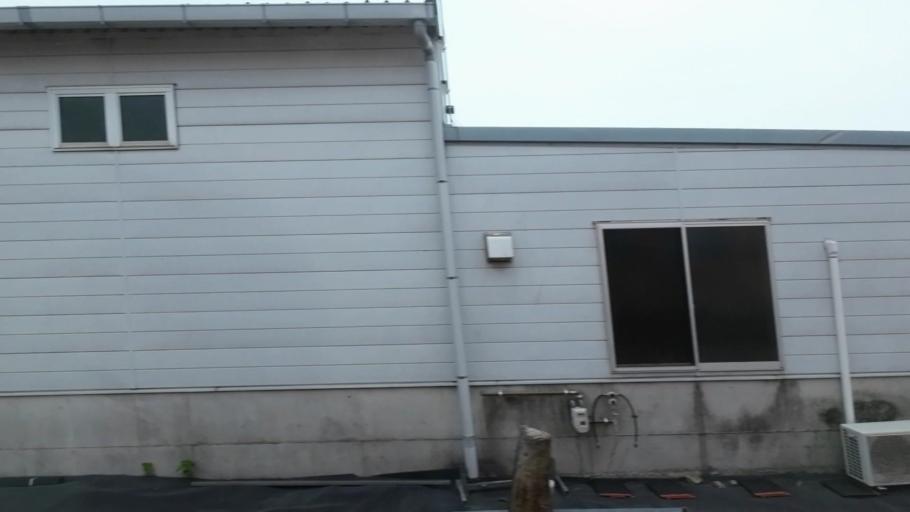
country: JP
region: Kochi
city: Kochi-shi
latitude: 33.6020
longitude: 133.6743
